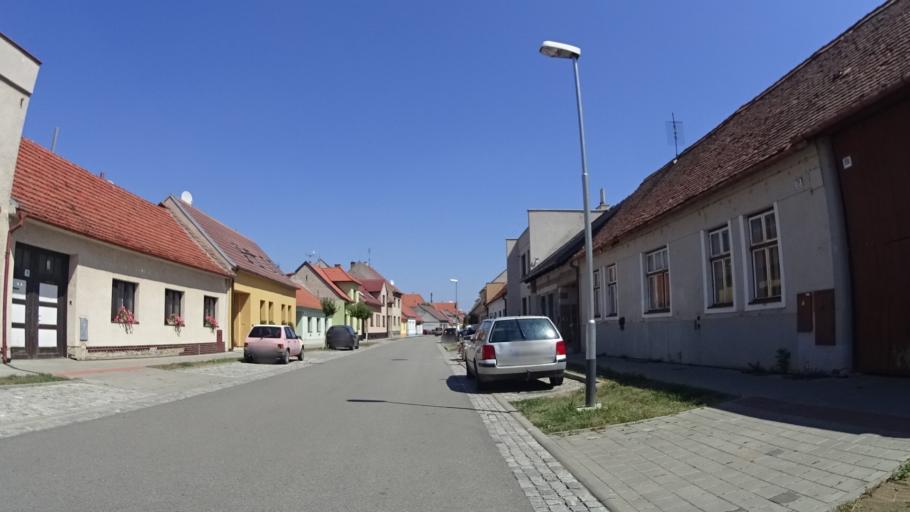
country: CZ
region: South Moravian
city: Straznice
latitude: 48.8992
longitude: 17.3089
